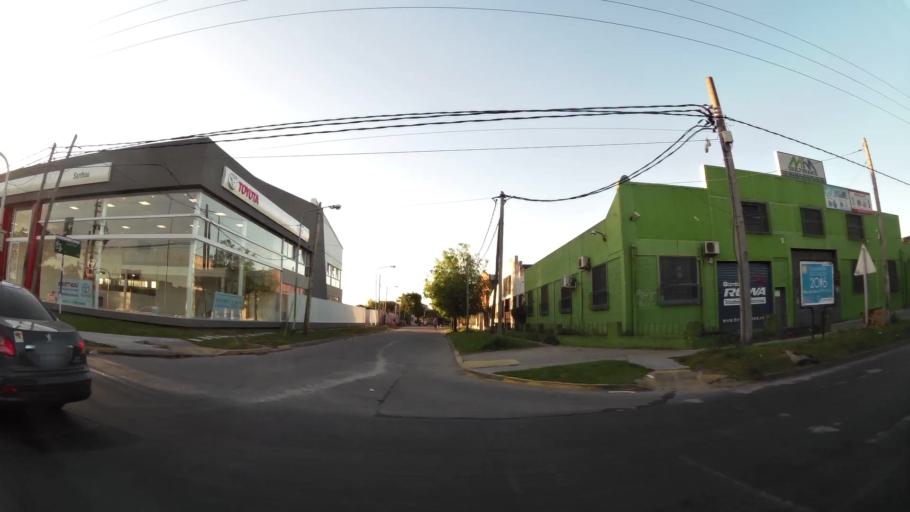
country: AR
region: Buenos Aires
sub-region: Partido de Tigre
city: Tigre
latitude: -34.4388
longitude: -58.5724
